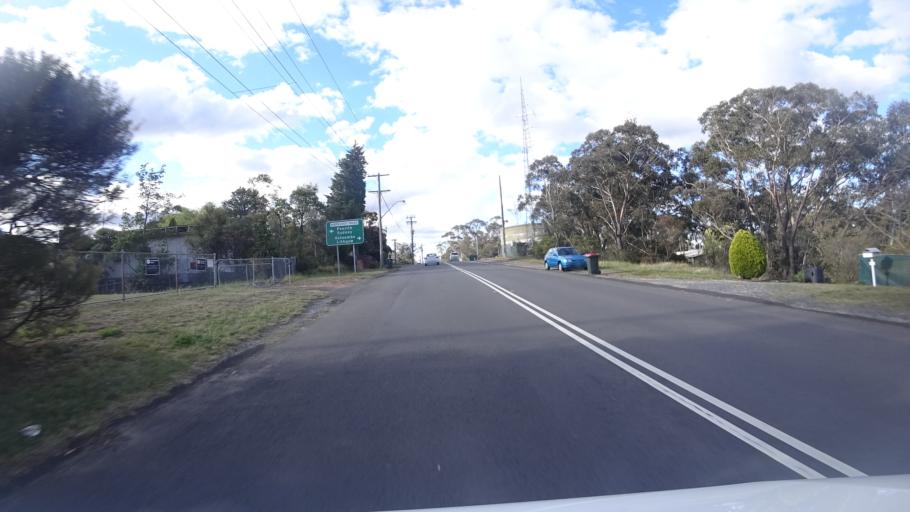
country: AU
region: New South Wales
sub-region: Blue Mountains Municipality
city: Katoomba
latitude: -33.7105
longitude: 150.3000
